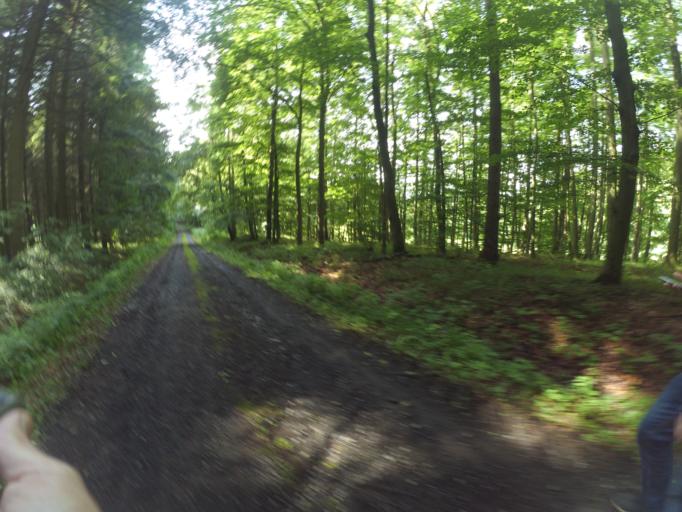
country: DE
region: Hesse
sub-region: Regierungsbezirk Kassel
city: Kirchheim
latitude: 50.8800
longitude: 9.5275
